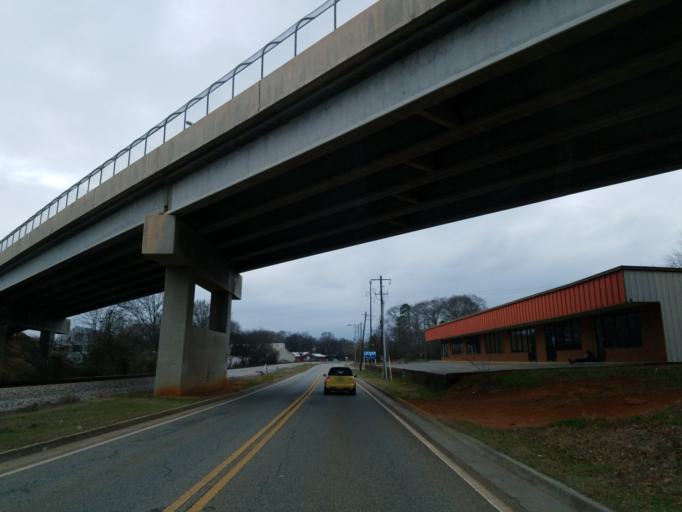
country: US
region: Georgia
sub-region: Bartow County
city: Cartersville
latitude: 34.1573
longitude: -84.7908
